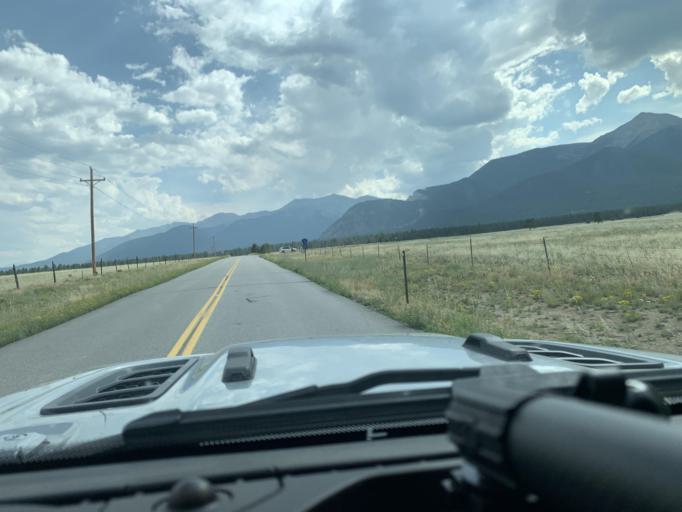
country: US
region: Colorado
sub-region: Chaffee County
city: Buena Vista
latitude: 38.7606
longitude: -106.1504
